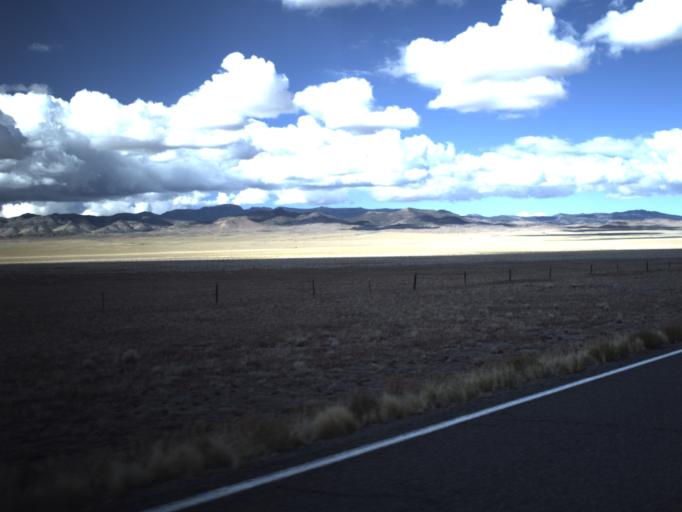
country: US
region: Utah
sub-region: Beaver County
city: Milford
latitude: 38.5516
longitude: -113.7340
